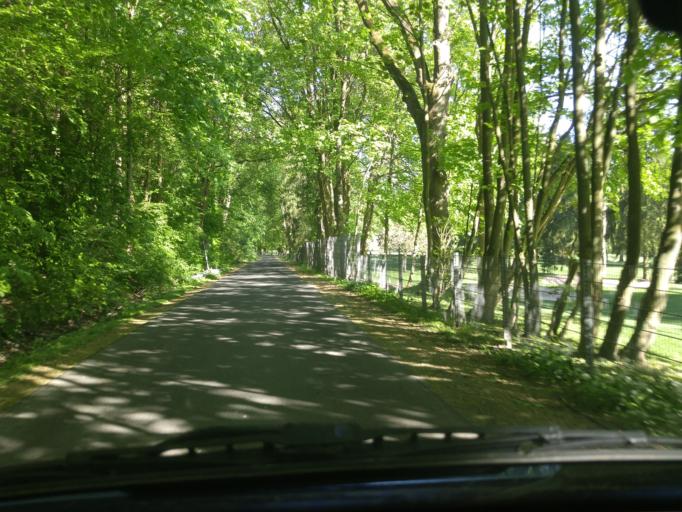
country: DE
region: Hesse
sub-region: Regierungsbezirk Darmstadt
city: Bad Nauheim
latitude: 50.3728
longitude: 8.7359
